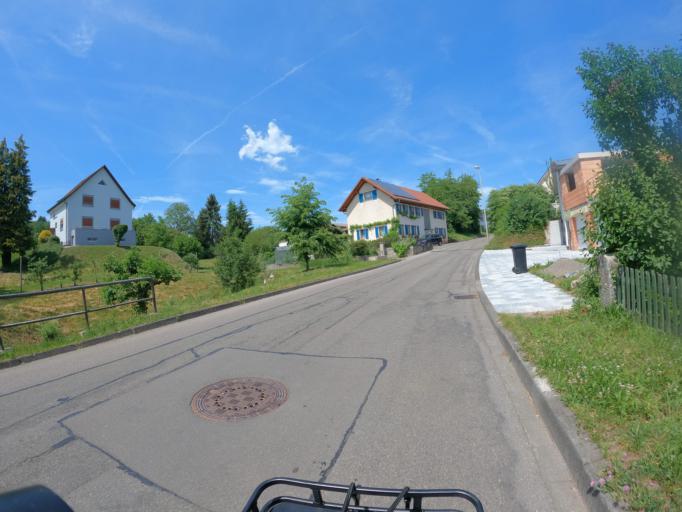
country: CH
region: Zurich
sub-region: Bezirk Andelfingen
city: Dachsen
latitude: 47.6559
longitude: 8.5990
